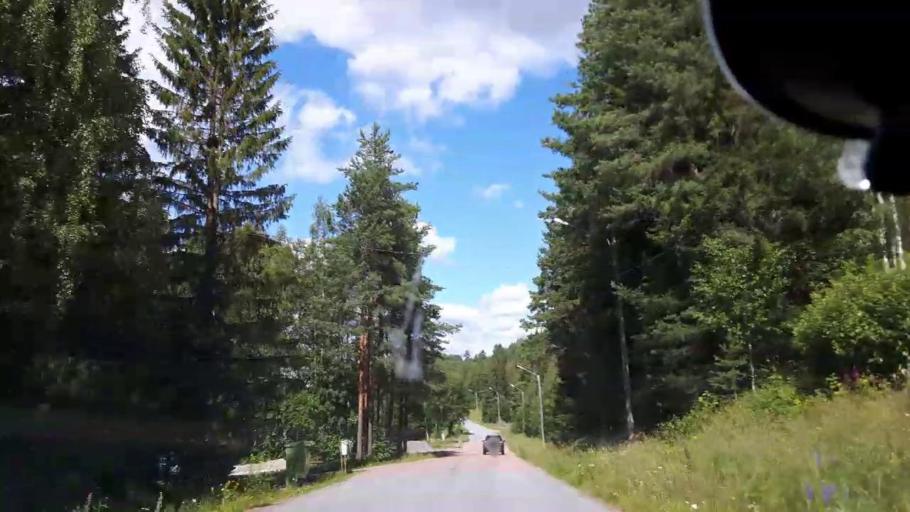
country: SE
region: Jaemtland
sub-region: Ragunda Kommun
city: Hammarstrand
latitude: 62.9459
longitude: 16.6896
